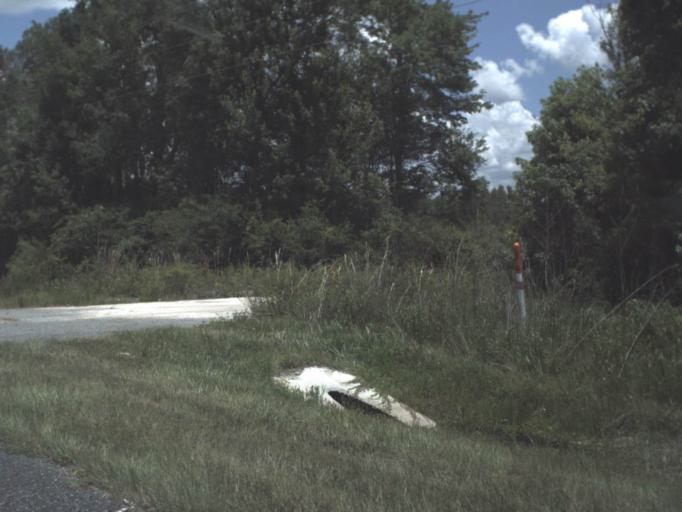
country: US
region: Florida
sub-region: Taylor County
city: Perry
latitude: 29.9377
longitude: -83.4473
